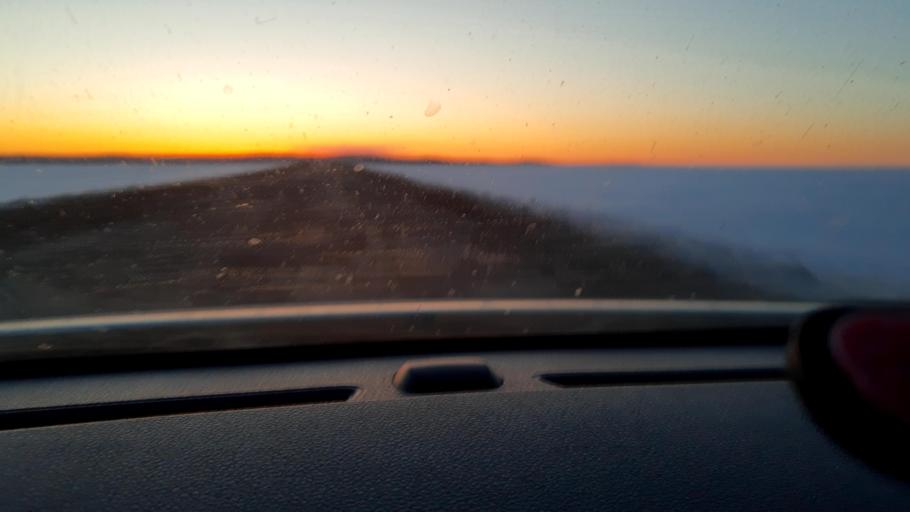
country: RU
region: Bashkortostan
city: Avdon
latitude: 54.3879
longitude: 55.7714
